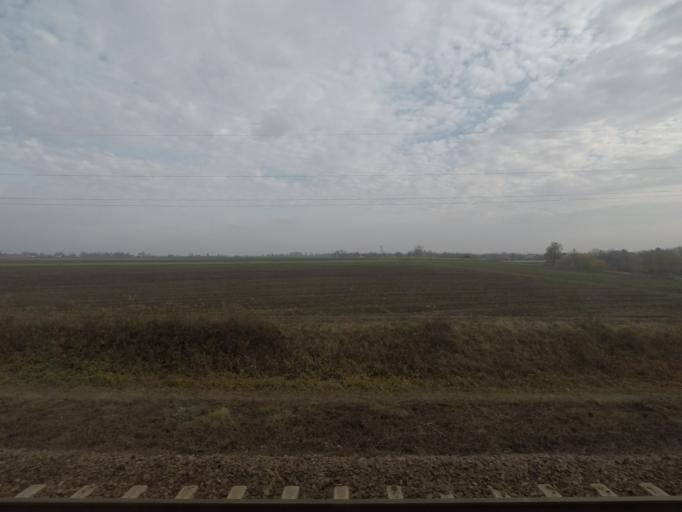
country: PL
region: Subcarpathian Voivodeship
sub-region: Powiat jaroslawski
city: Sosnica
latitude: 49.8693
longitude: 22.8609
